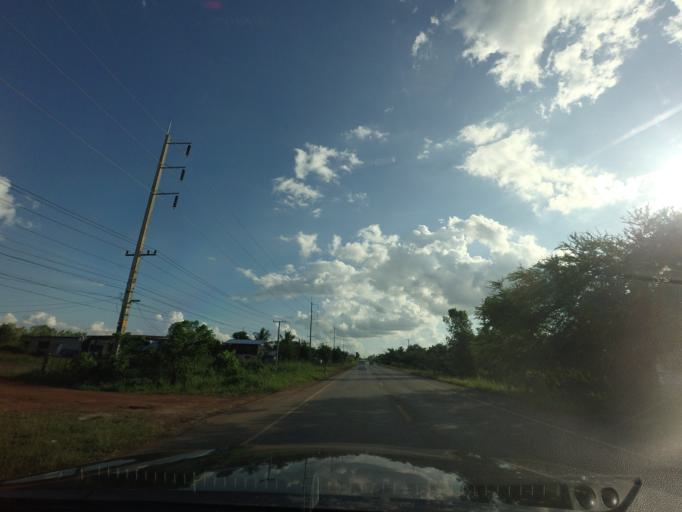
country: TH
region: Changwat Udon Thani
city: Thung Fon
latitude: 17.4974
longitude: 103.2019
